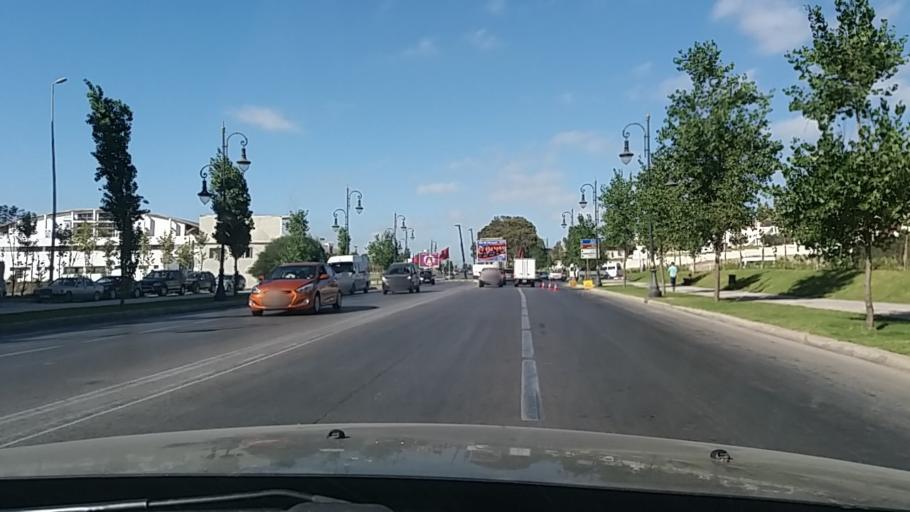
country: MA
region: Tanger-Tetouan
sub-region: Tanger-Assilah
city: Boukhalef
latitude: 35.7472
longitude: -5.8600
